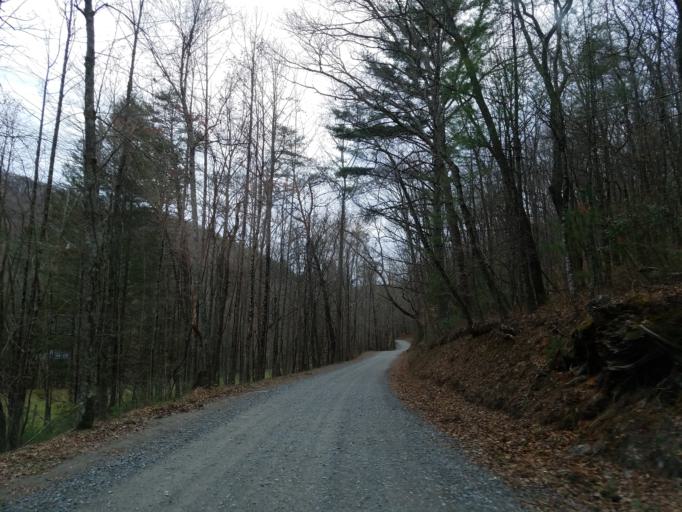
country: US
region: Georgia
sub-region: Fannin County
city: Blue Ridge
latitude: 34.7503
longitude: -84.2761
